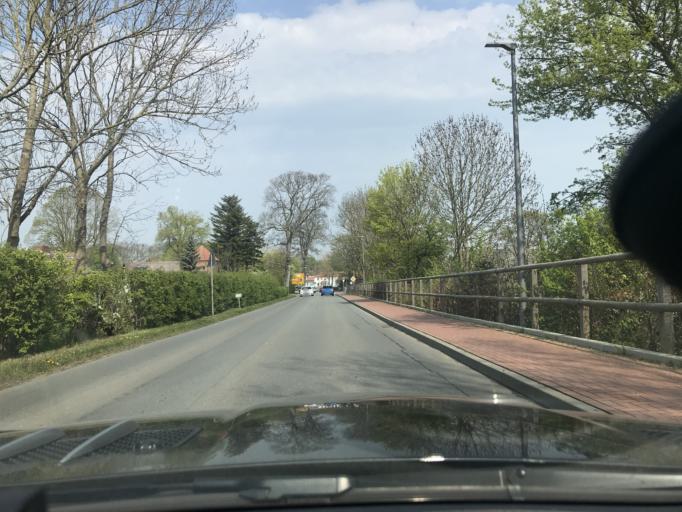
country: DE
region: Schleswig-Holstein
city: Heiligenhafen
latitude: 54.3694
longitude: 10.9711
